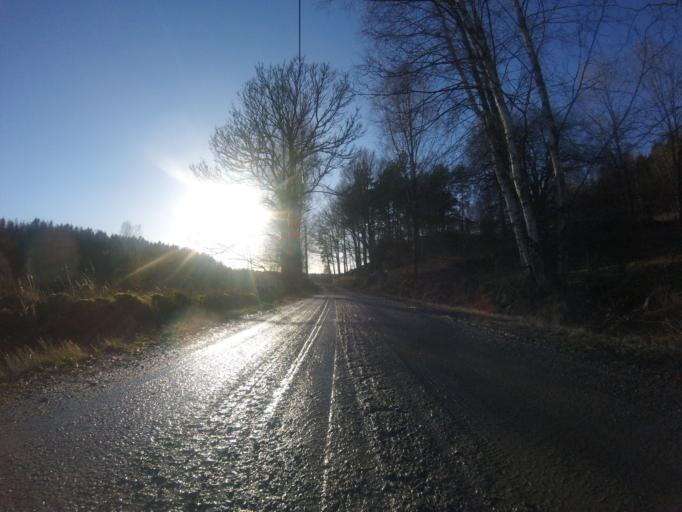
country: SE
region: Halland
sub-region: Varbergs Kommun
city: Veddige
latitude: 57.2282
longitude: 12.3023
